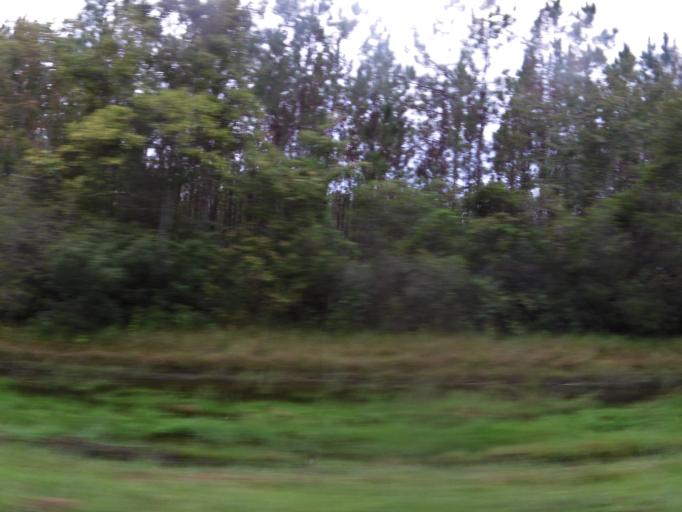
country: US
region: Florida
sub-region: Duval County
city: Baldwin
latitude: 30.3966
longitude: -81.9523
